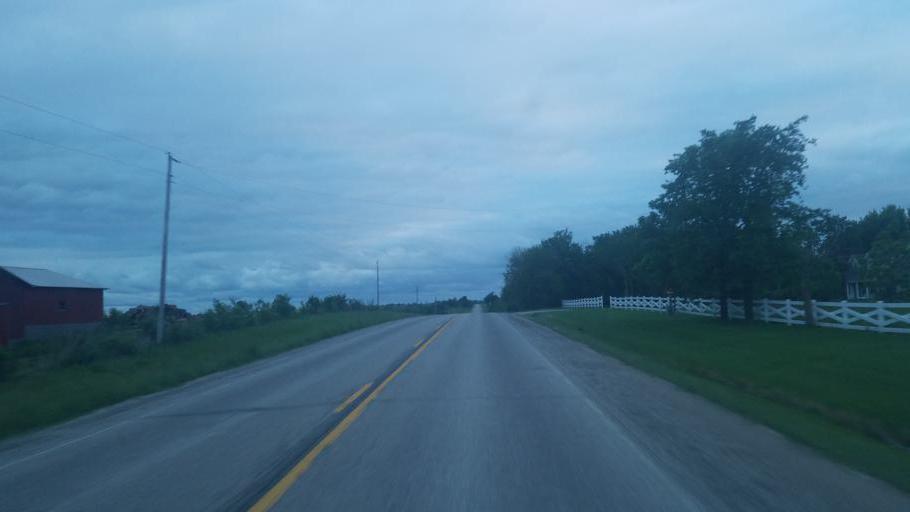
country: US
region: Iowa
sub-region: Decatur County
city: Lamoni
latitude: 40.5916
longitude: -93.9389
